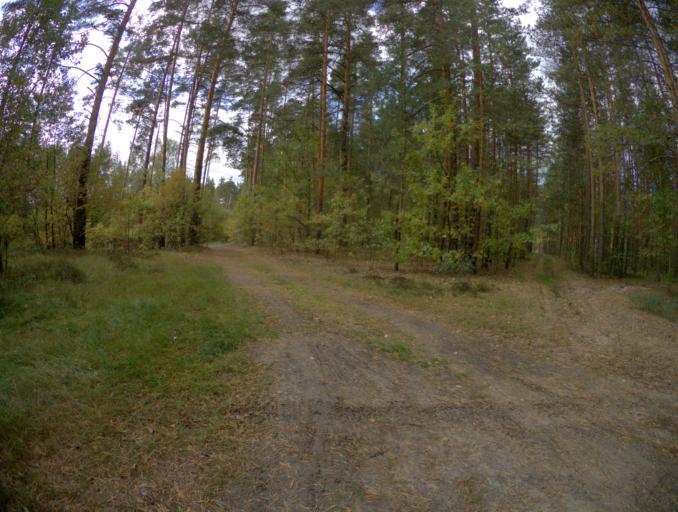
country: RU
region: Moskovskaya
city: Baksheyevo
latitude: 55.7368
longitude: 39.8220
